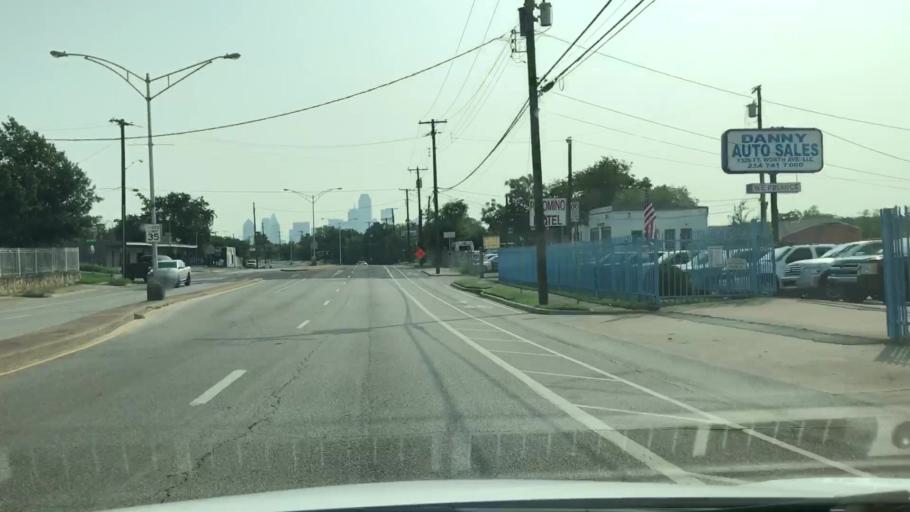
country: US
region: Texas
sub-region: Dallas County
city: Dallas
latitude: 32.7662
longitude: -96.8425
